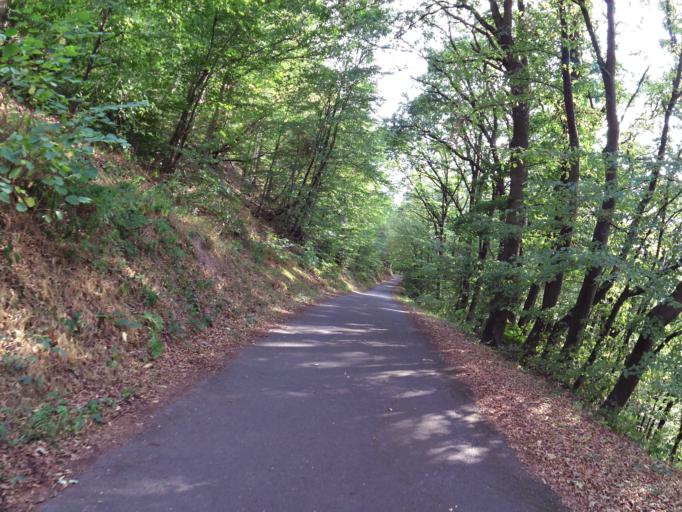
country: DE
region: North Rhine-Westphalia
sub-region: Regierungsbezirk Koln
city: Nideggen
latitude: 50.6832
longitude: 6.4737
